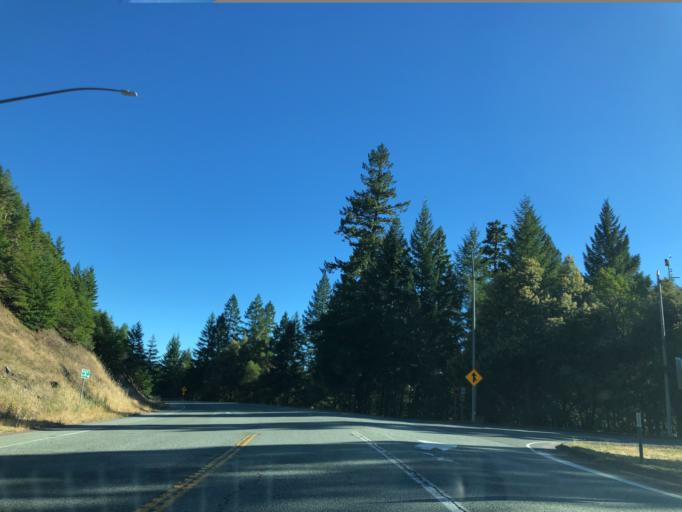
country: US
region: Oregon
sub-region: Josephine County
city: Cave Junction
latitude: 41.9677
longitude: -123.7471
